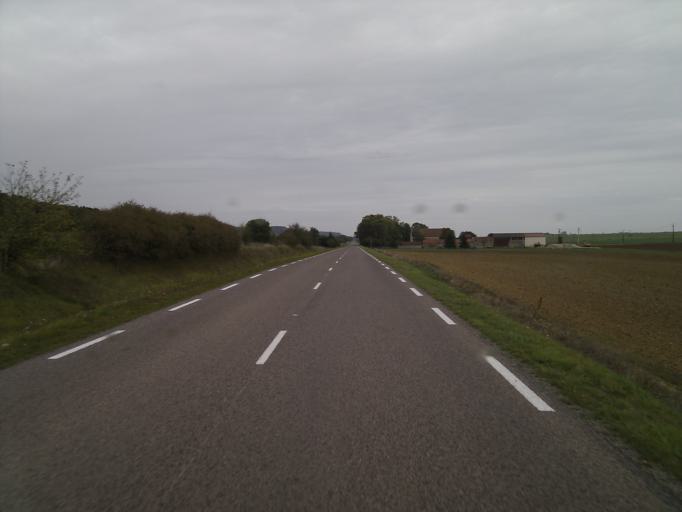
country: FR
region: Champagne-Ardenne
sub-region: Departement de la Haute-Marne
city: Doulaincourt-Saucourt
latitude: 48.2576
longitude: 5.3677
